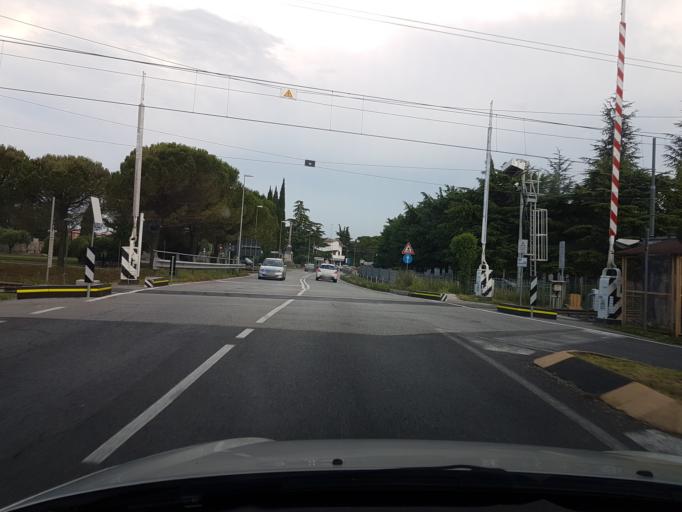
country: IT
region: Friuli Venezia Giulia
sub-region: Provincia di Gorizia
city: Ronchi dei Legionari
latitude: 45.8217
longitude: 13.5123
